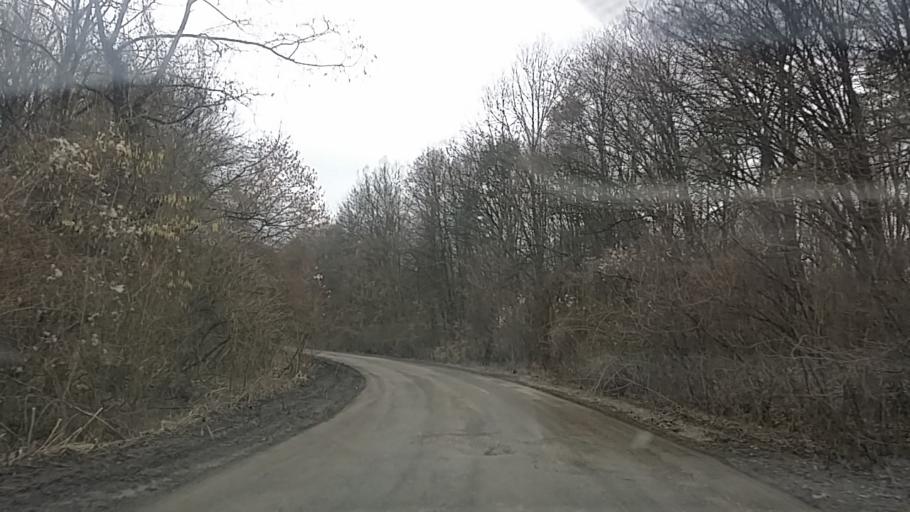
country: HU
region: Borsod-Abauj-Zemplen
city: Rudabanya
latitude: 48.4015
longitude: 20.6579
